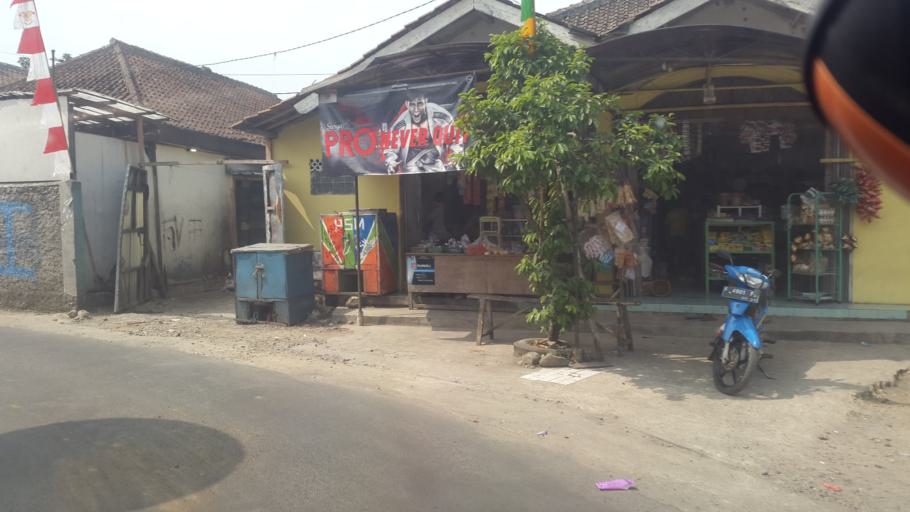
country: ID
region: West Java
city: Cicurug
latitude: -6.7594
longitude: 106.7716
